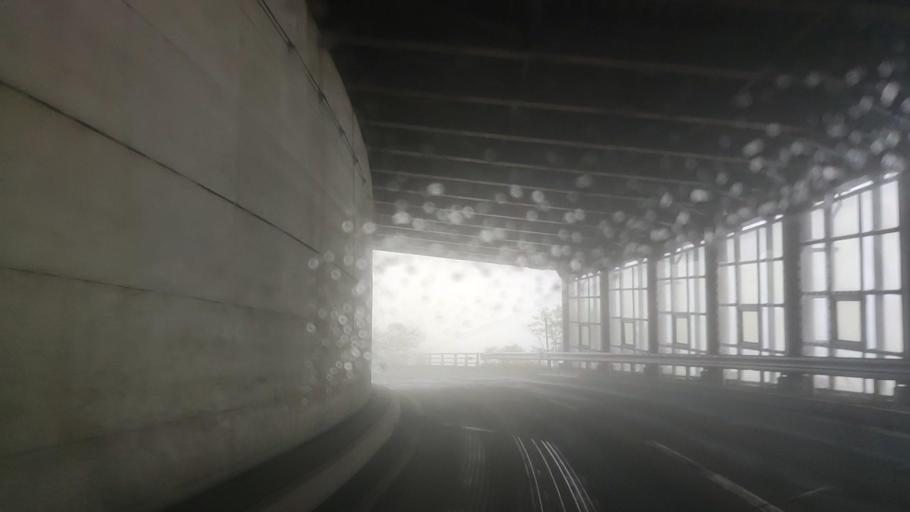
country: JP
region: Hokkaido
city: Date
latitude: 42.5497
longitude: 141.0848
